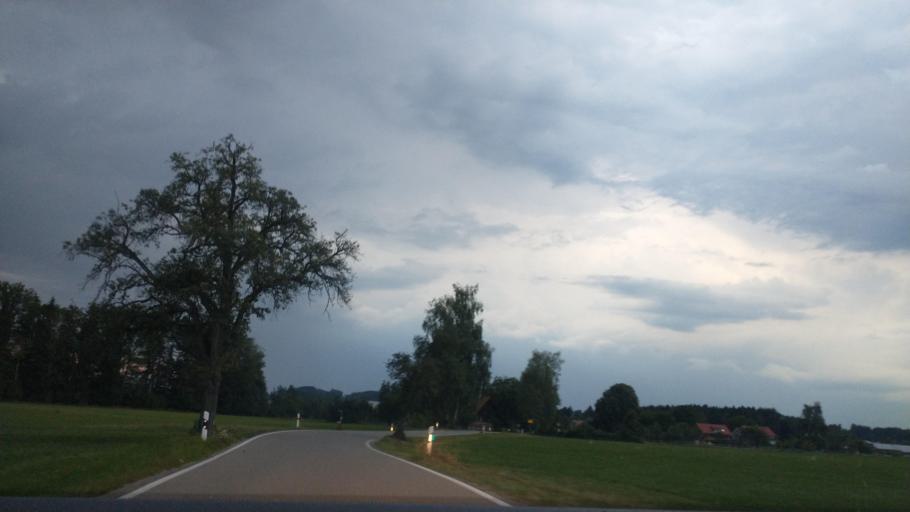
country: DE
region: Baden-Wuerttemberg
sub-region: Tuebingen Region
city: Amtzell
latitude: 47.6949
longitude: 9.7474
